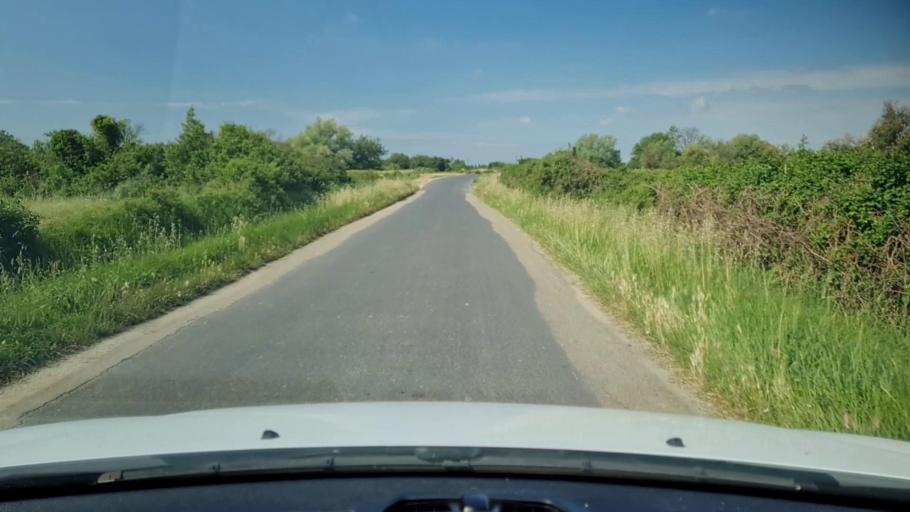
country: FR
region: Languedoc-Roussillon
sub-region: Departement du Gard
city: Le Cailar
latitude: 43.6677
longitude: 4.2335
